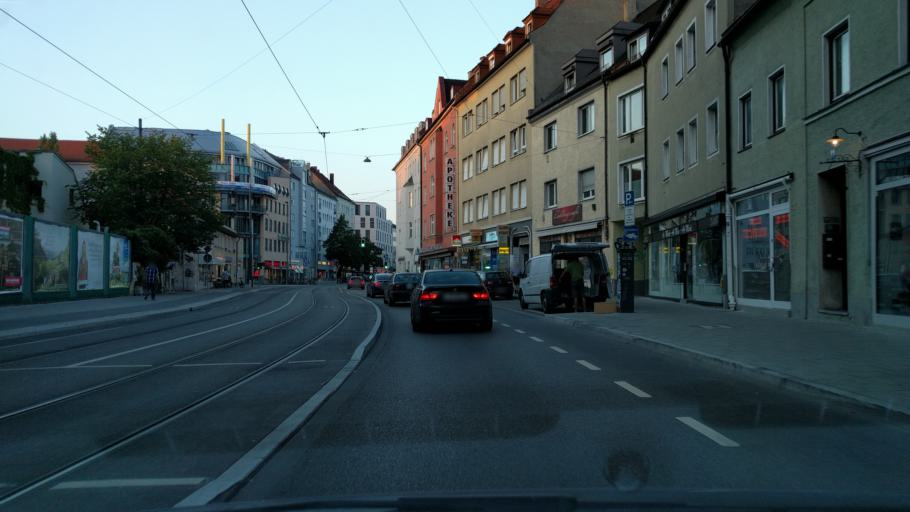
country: DE
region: Bavaria
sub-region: Upper Bavaria
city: Munich
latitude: 48.1143
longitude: 11.5789
